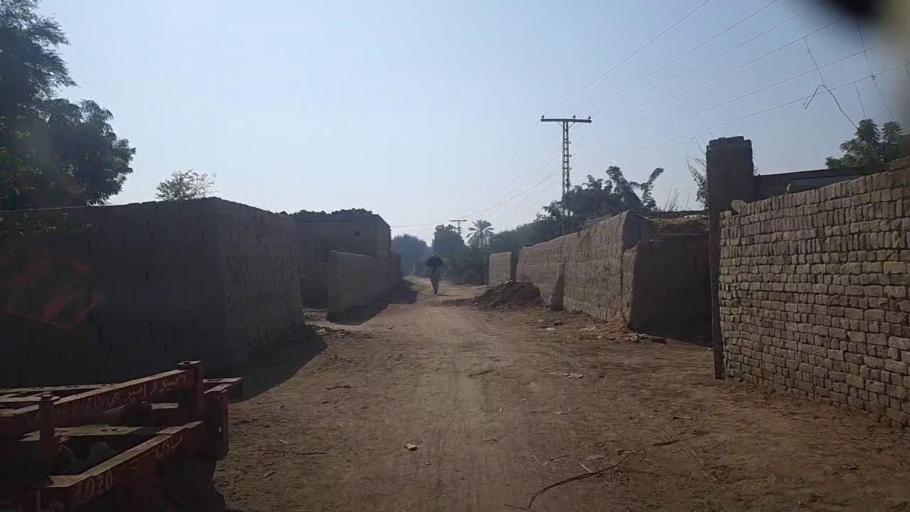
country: PK
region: Sindh
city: Kandiari
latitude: 27.0214
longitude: 68.5078
